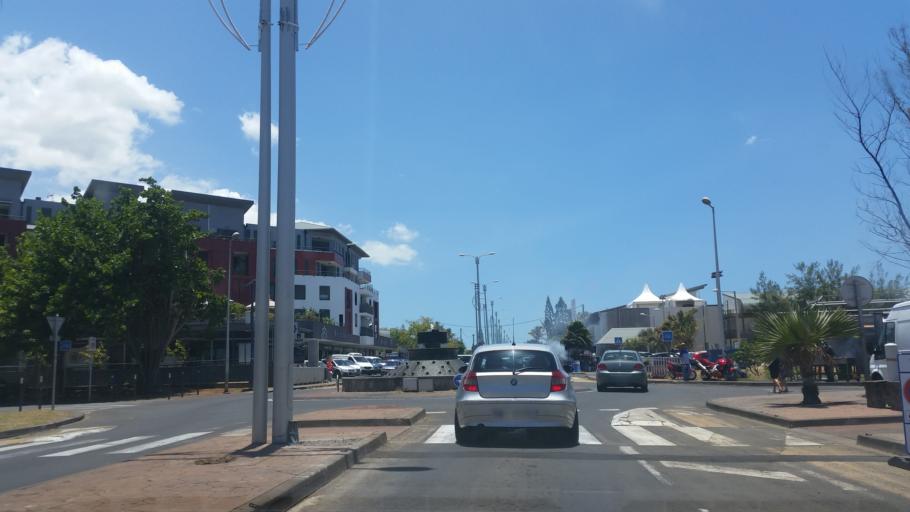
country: RE
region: Reunion
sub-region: Reunion
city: Saint-Pierre
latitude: -21.3406
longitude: 55.4608
